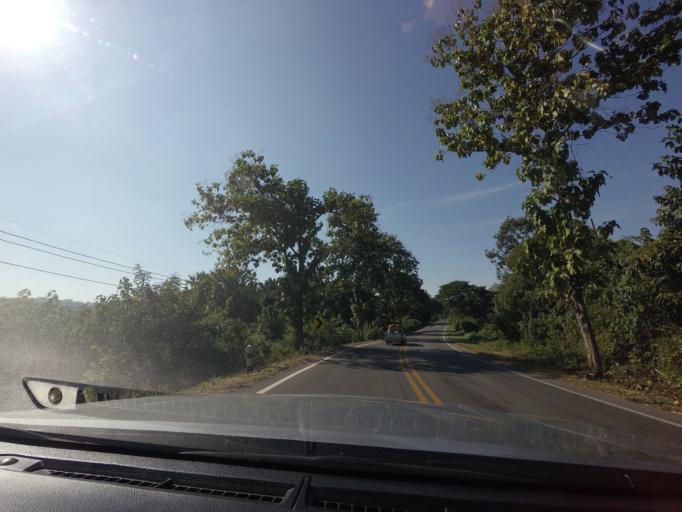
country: TH
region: Sukhothai
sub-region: Amphoe Si Satchanalai
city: Si Satchanalai
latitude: 17.6062
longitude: 99.7110
